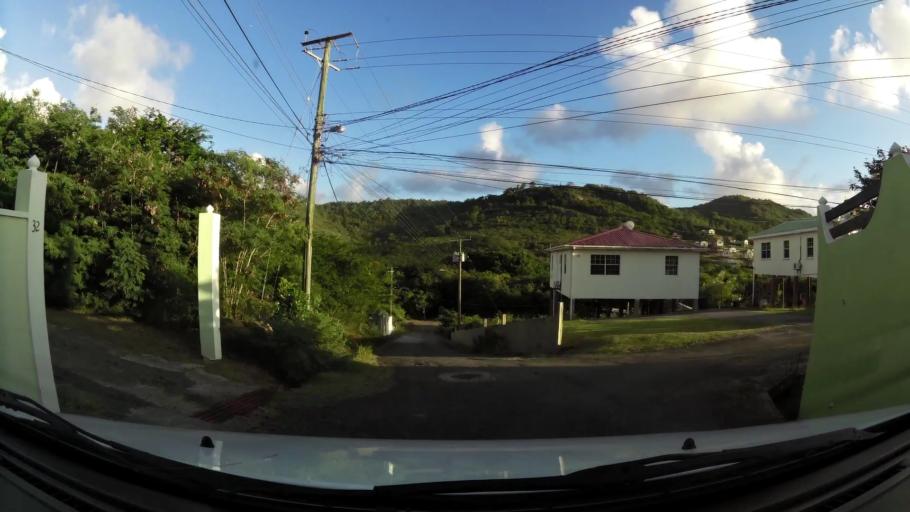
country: LC
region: Gros-Islet
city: Gros Islet
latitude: 14.0749
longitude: -60.9277
